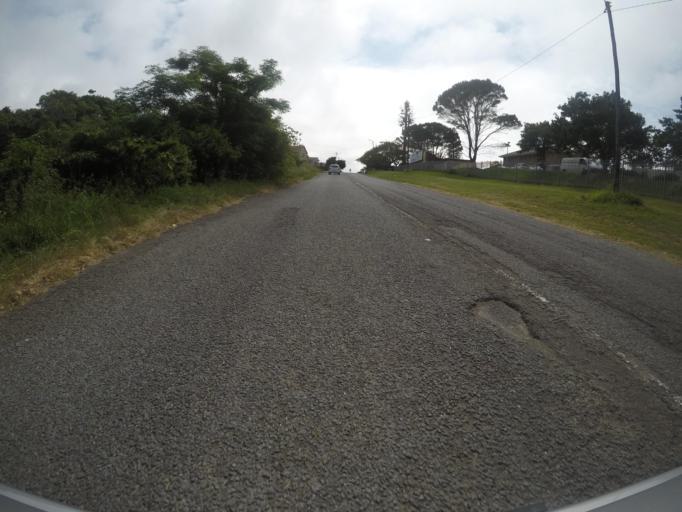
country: ZA
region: Eastern Cape
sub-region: Buffalo City Metropolitan Municipality
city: East London
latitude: -32.9959
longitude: 27.9120
